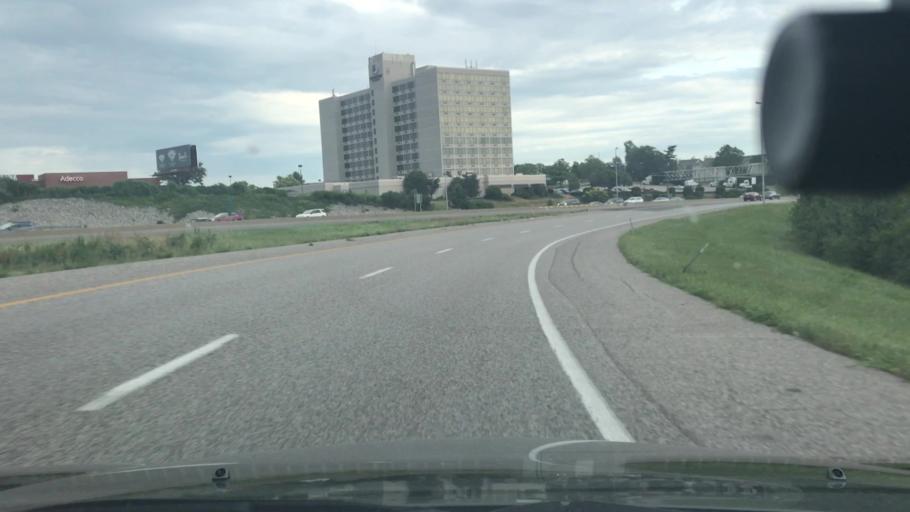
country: US
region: Missouri
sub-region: Saint Louis County
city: Maryland Heights
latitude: 38.6956
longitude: -90.4514
